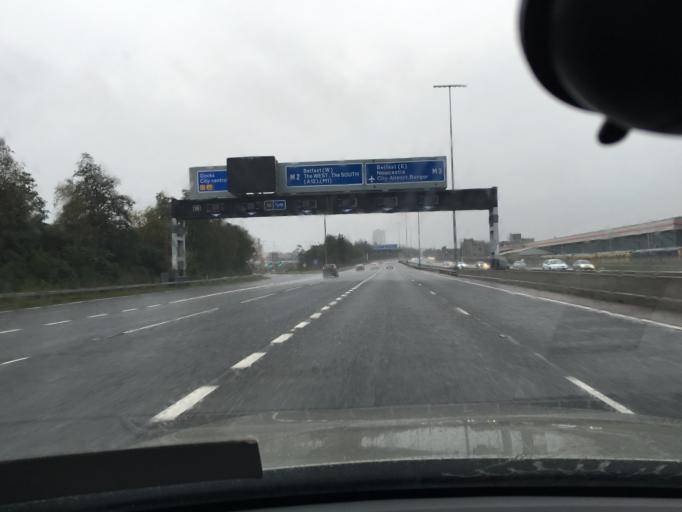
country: GB
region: Northern Ireland
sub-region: City of Belfast
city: Belfast
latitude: 54.6147
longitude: -5.9210
